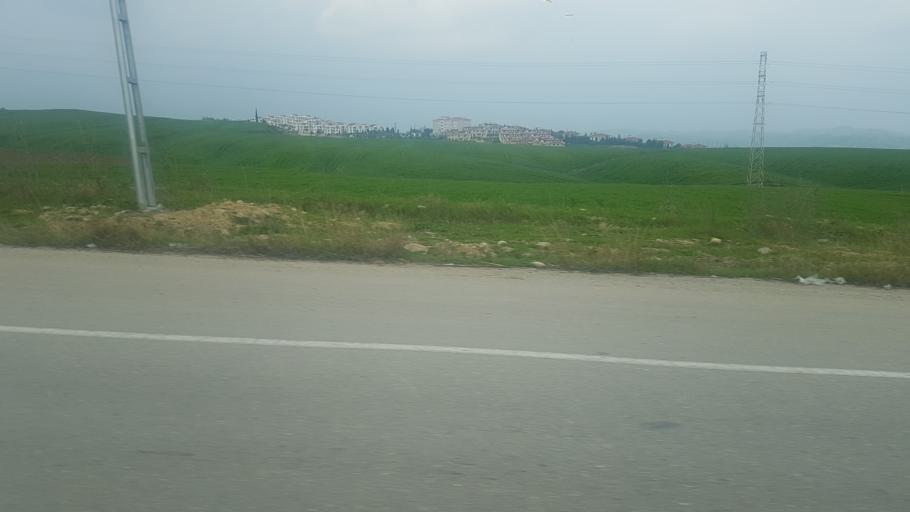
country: TR
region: Adana
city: Seyhan
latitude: 37.0585
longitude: 35.2358
